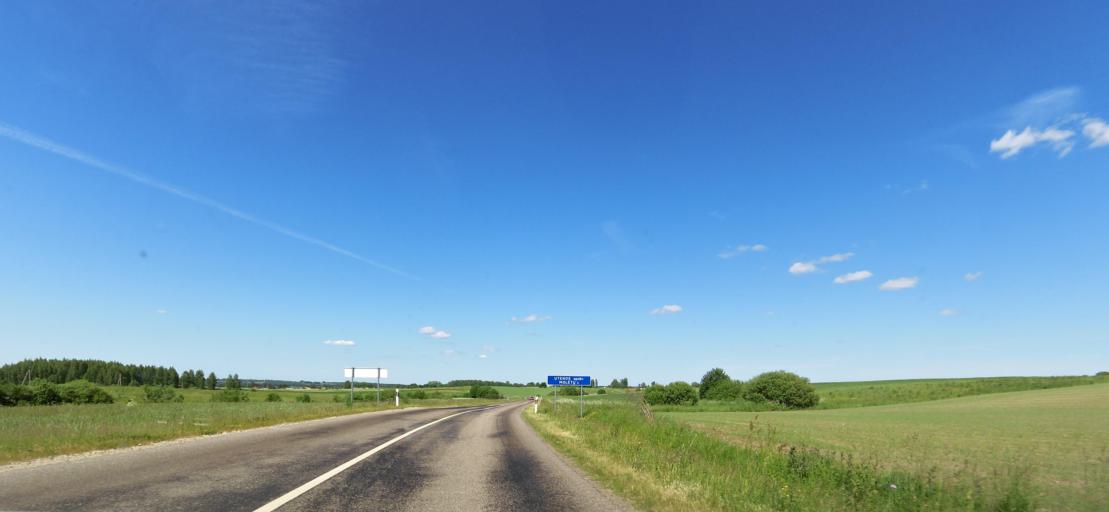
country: LT
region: Utenos apskritis
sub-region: Anyksciai
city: Anyksciai
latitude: 55.2766
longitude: 25.1085
